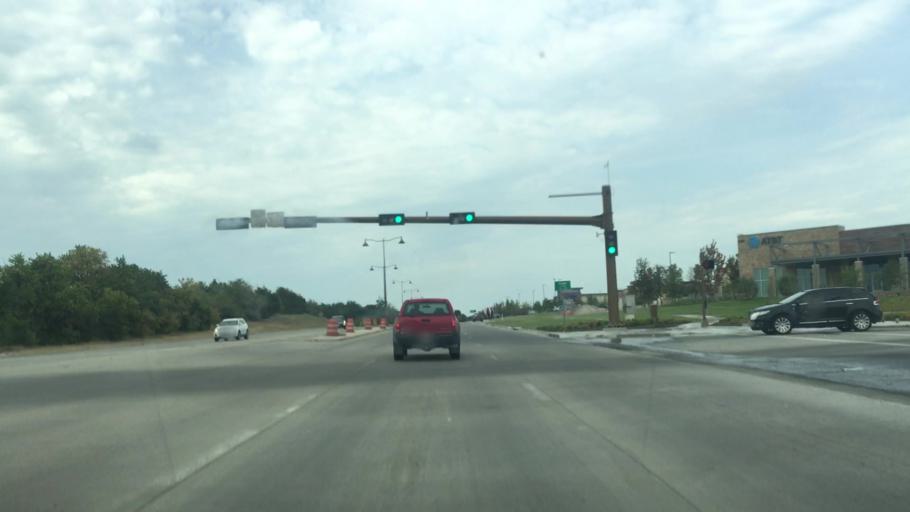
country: US
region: Texas
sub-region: Collin County
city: Prosper
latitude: 33.2234
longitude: -96.7984
